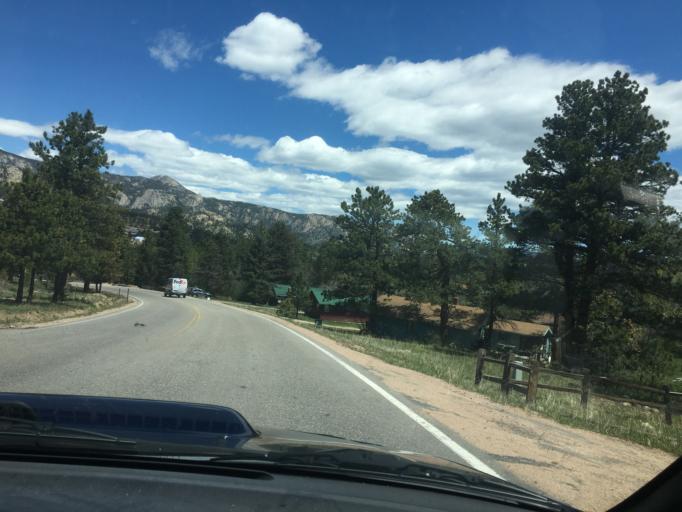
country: US
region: Colorado
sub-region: Larimer County
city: Estes Park
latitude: 40.3577
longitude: -105.5412
